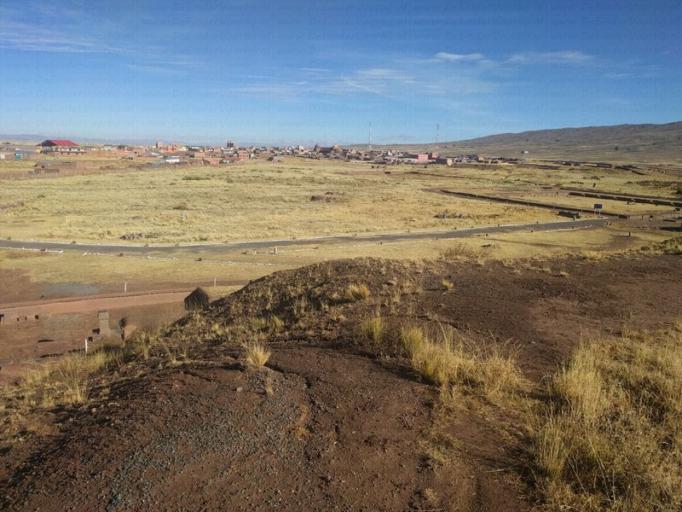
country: BO
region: La Paz
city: Tiahuanaco
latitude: -16.5563
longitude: -68.6734
